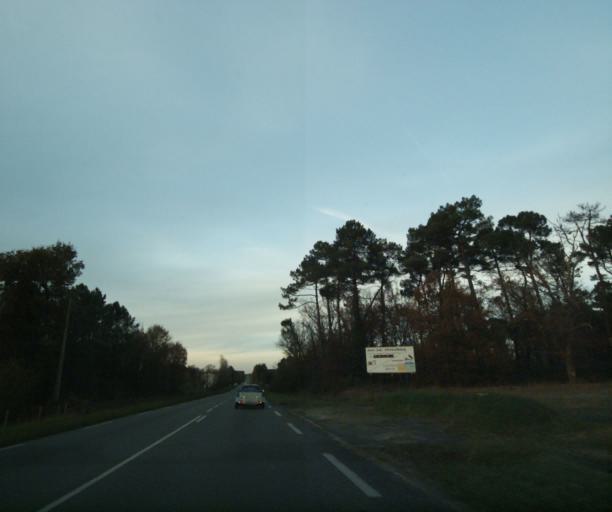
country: FR
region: Aquitaine
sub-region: Departement de la Gironde
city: Bazas
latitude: 44.4837
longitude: -0.2312
